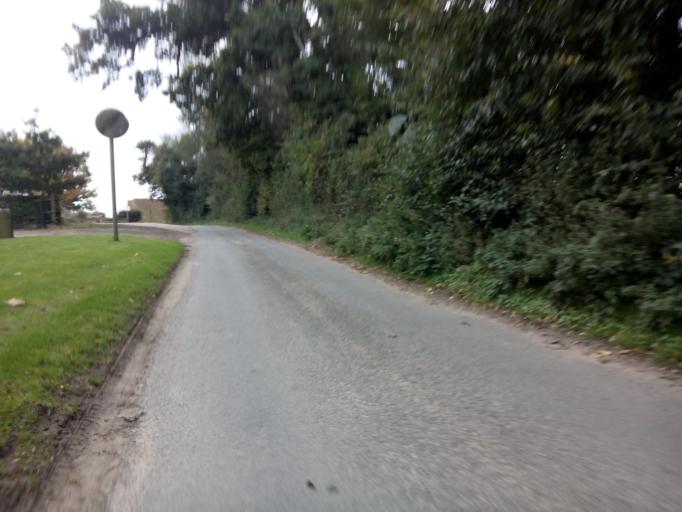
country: GB
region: England
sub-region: Suffolk
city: Ipswich
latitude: 52.0208
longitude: 1.1411
